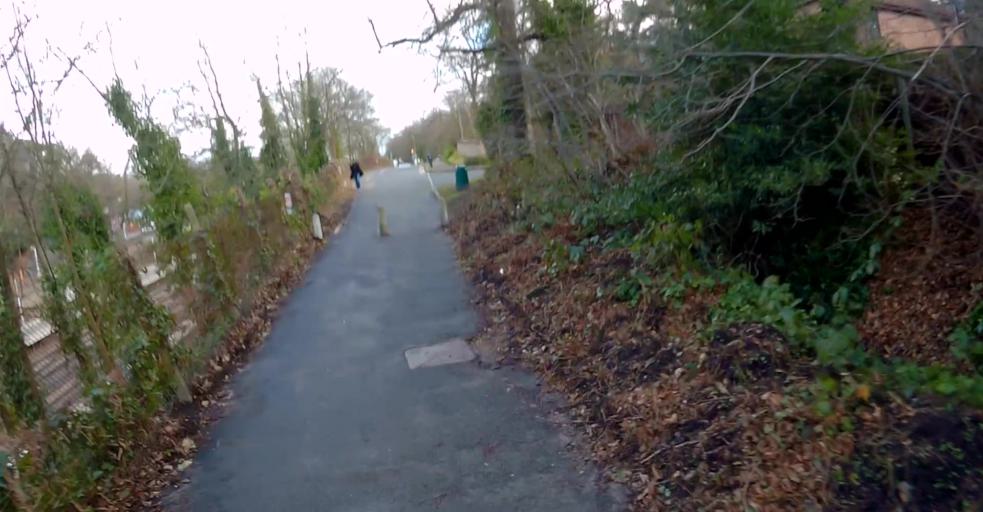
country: GB
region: England
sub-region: Surrey
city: Weybridge
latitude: 51.3607
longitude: -0.4591
